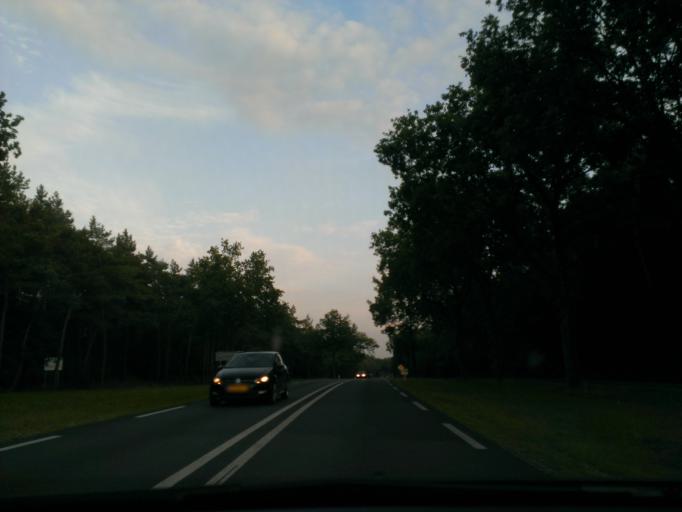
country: NL
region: Gelderland
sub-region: Gemeente Oldebroek
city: Oldebroek
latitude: 52.3860
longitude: 5.9102
